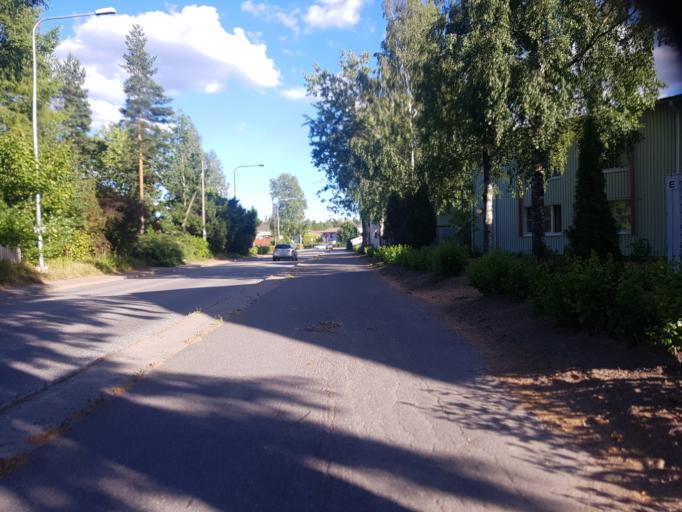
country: FI
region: Uusimaa
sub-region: Helsinki
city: Vantaa
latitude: 60.2699
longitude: 25.0080
